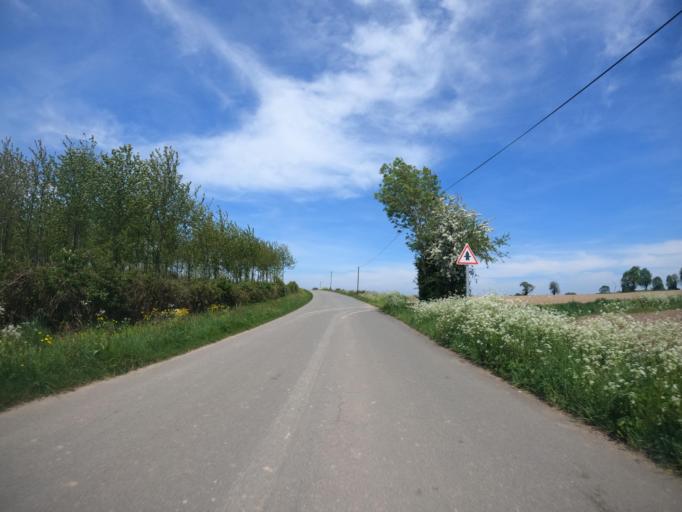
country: FR
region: Poitou-Charentes
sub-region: Departement des Deux-Sevres
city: La Chapelle-Saint-Laurent
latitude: 46.6541
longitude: -0.5067
